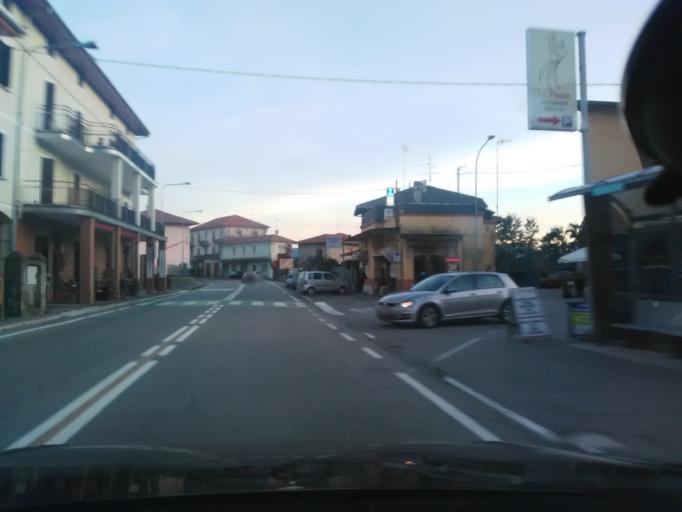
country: IT
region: Piedmont
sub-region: Provincia di Novara
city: Grignasco
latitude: 45.6815
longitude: 8.3378
